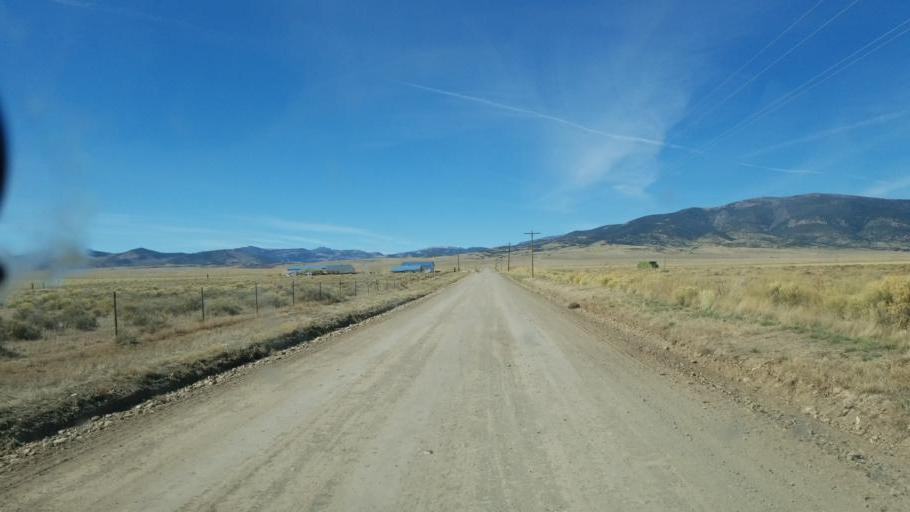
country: US
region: Colorado
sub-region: Rio Grande County
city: Monte Vista
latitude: 37.4011
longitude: -106.1420
